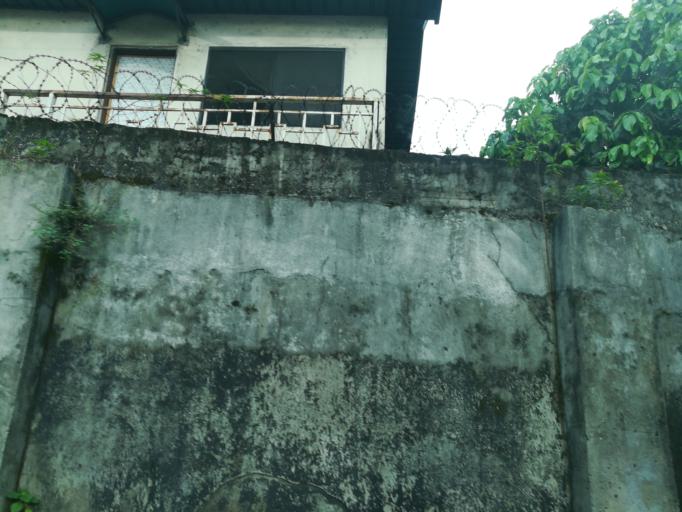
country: NG
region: Rivers
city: Port Harcourt
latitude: 4.8082
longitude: 6.9996
